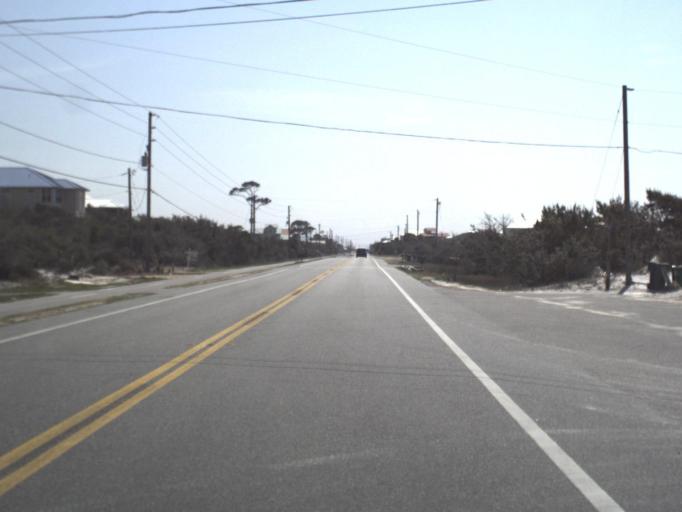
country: US
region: Florida
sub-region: Gulf County
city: Port Saint Joe
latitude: 29.6998
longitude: -85.3765
